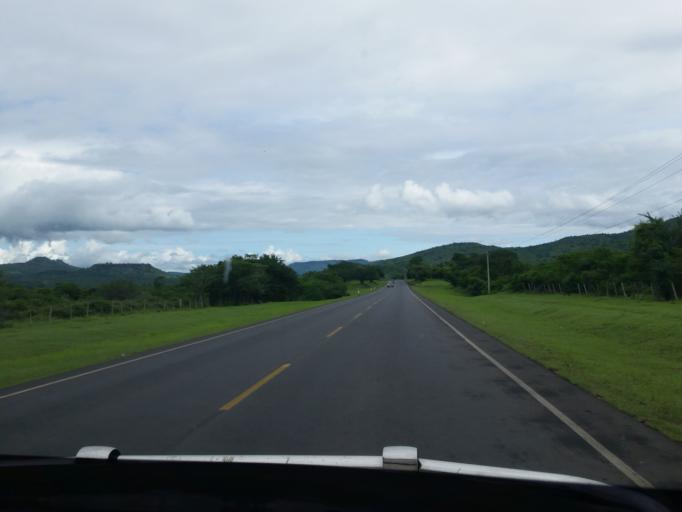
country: NI
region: Managua
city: Tipitapa
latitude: 12.4086
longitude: -86.0426
